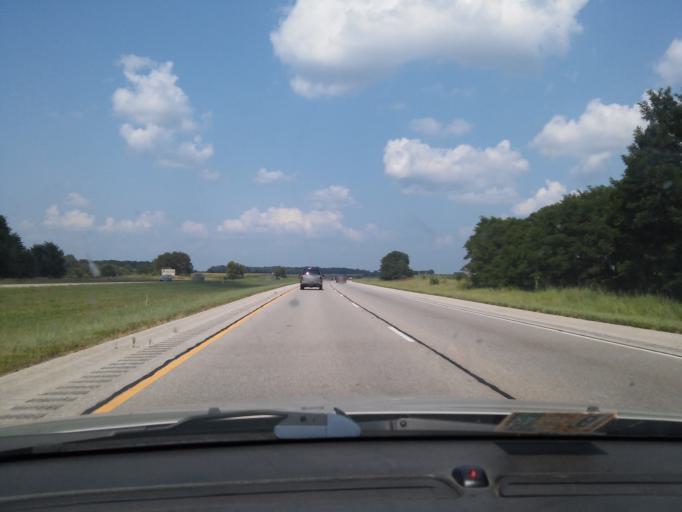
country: US
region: Illinois
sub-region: Logan County
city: Atlanta
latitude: 40.3441
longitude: -89.1334
